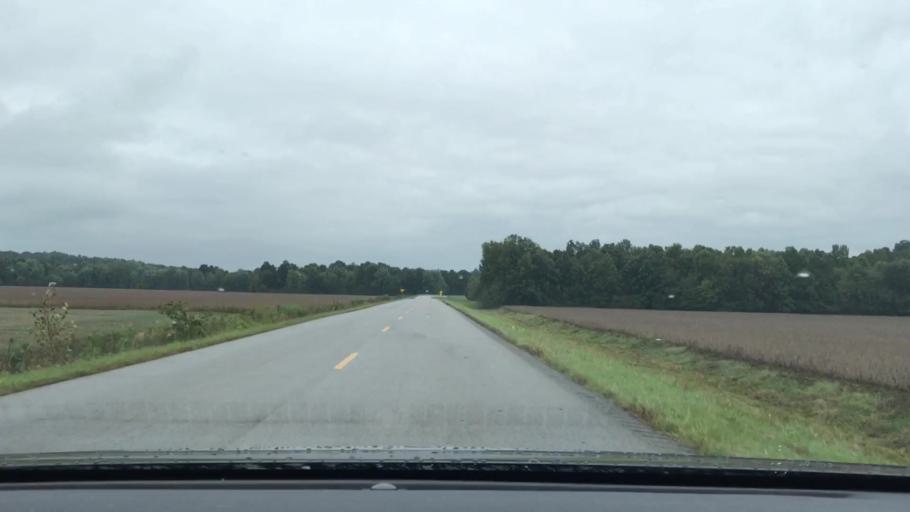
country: US
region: Kentucky
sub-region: McLean County
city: Calhoun
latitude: 37.4953
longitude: -87.2465
